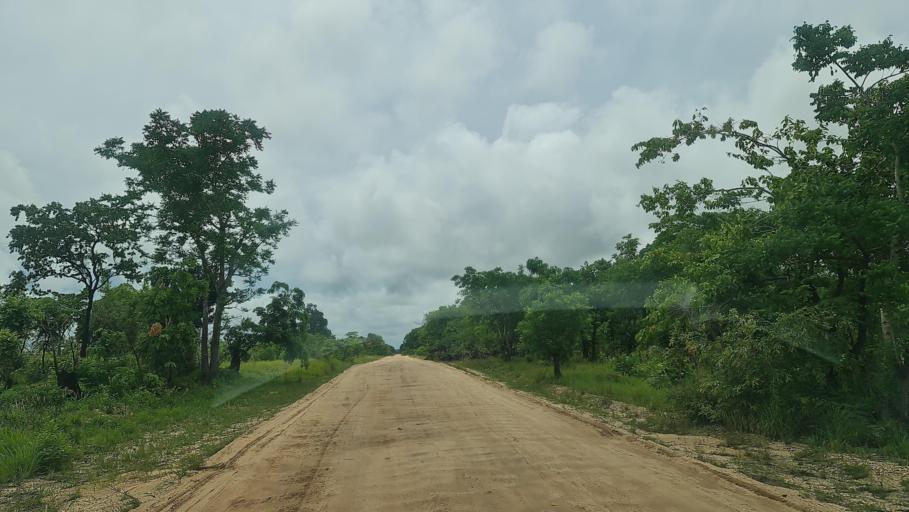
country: MZ
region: Zambezia
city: Quelimane
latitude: -17.2564
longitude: 37.2267
